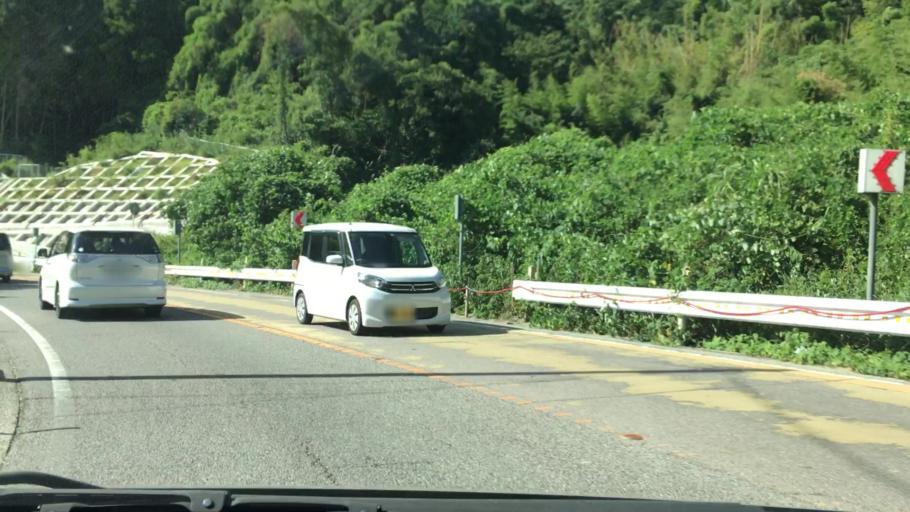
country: JP
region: Saga Prefecture
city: Takeocho-takeo
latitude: 33.1890
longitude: 129.9870
